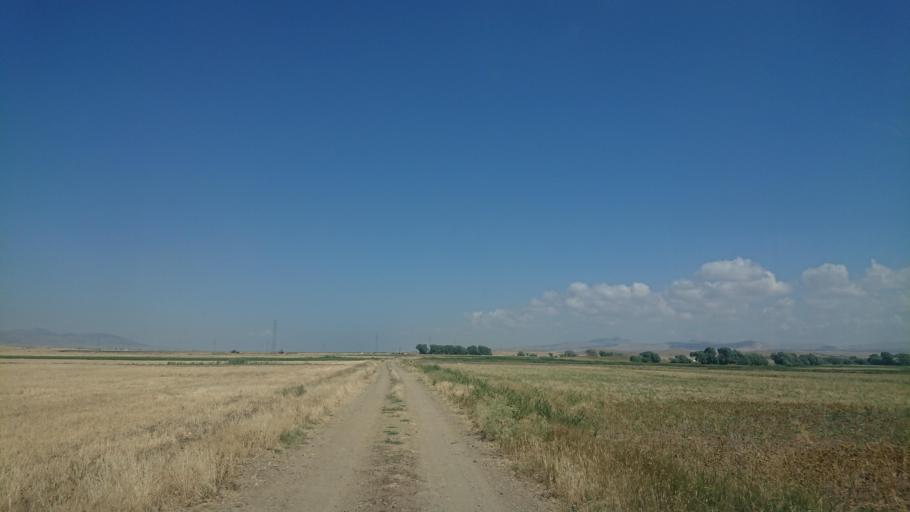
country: TR
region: Aksaray
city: Sariyahsi
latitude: 38.9904
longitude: 33.9001
